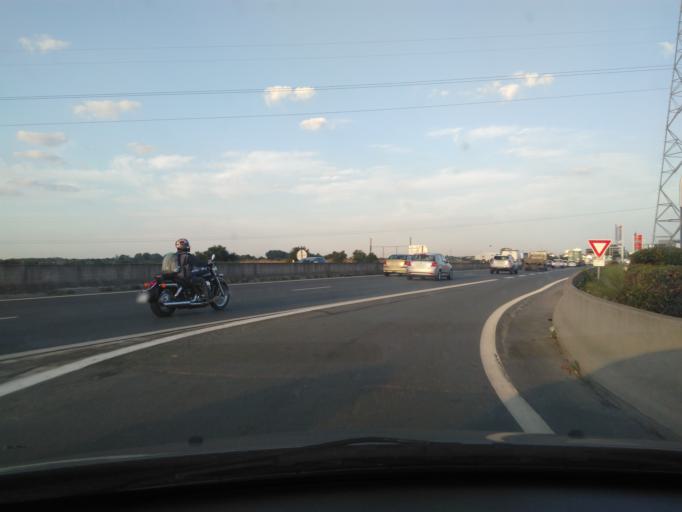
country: FR
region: Poitou-Charentes
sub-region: Departement de la Charente-Maritime
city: Puilboreau
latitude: 46.1760
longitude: -1.1076
